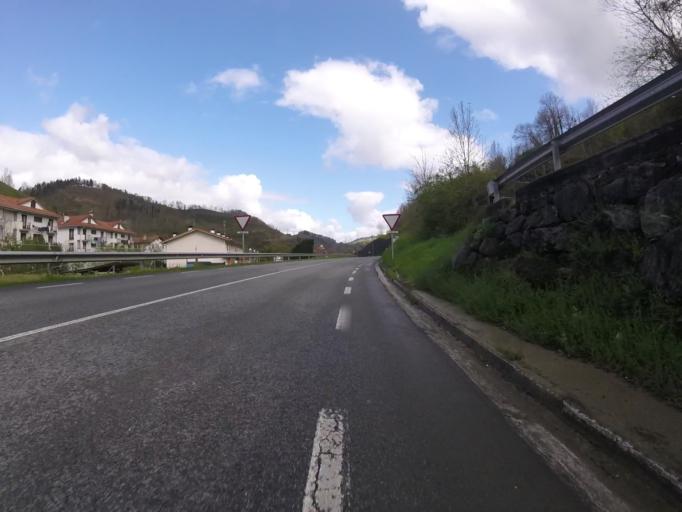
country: ES
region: Basque Country
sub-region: Provincia de Guipuzcoa
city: Amezqueta
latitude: 43.0514
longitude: -2.0884
